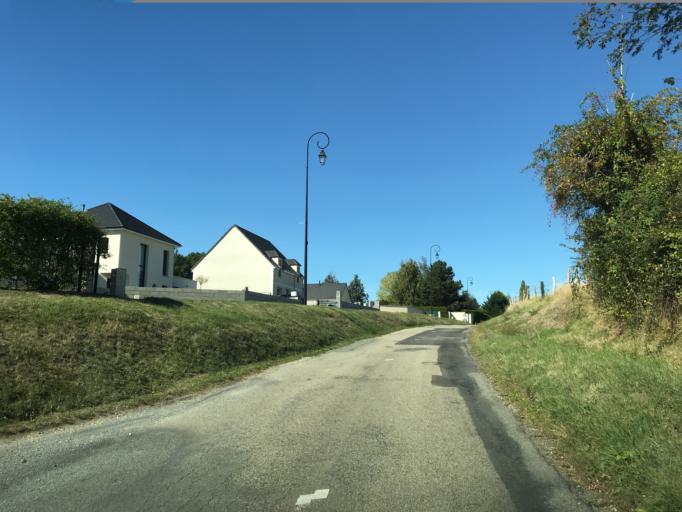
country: FR
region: Haute-Normandie
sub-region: Departement de l'Eure
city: Houlbec-Cocherel
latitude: 49.1009
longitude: 1.3358
